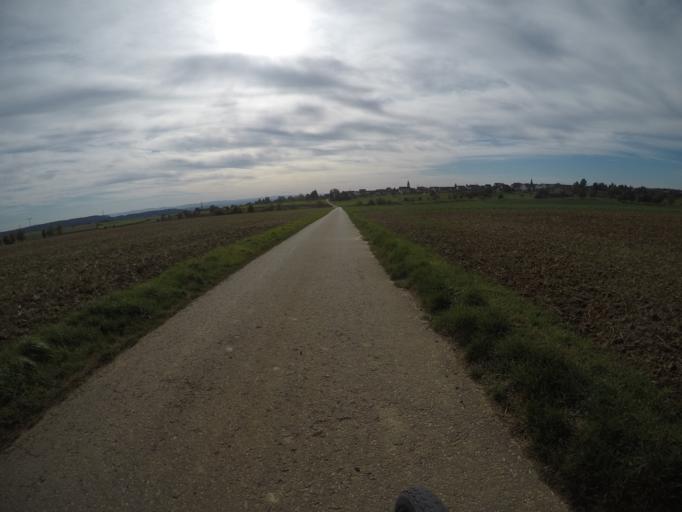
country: DE
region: Baden-Wuerttemberg
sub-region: Regierungsbezirk Stuttgart
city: Deckenpfronn
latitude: 48.6310
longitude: 8.8372
